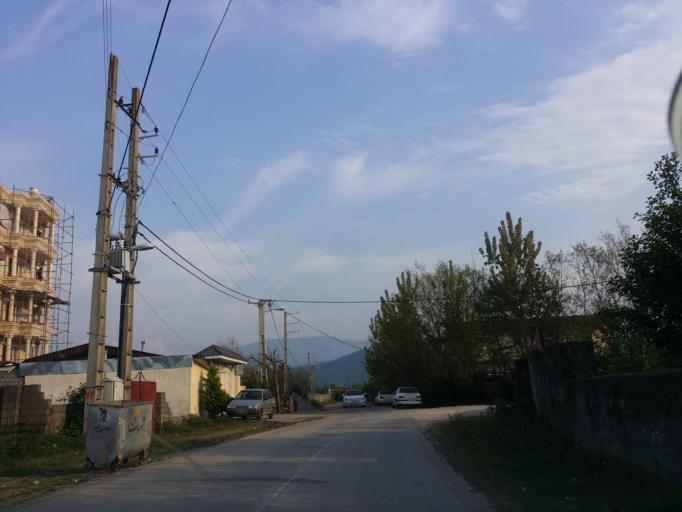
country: IR
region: Mazandaran
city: Chalus
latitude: 36.6790
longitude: 51.3723
